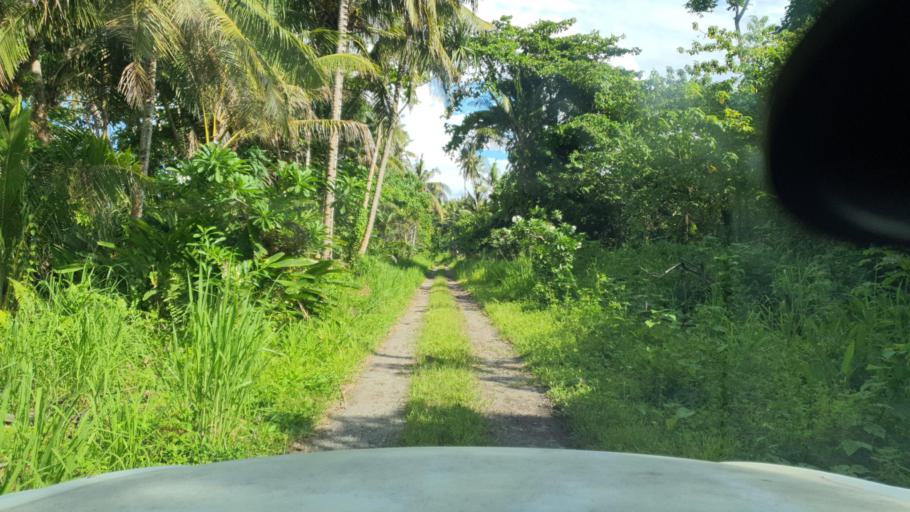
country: SB
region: Guadalcanal
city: Honiara
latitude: -9.2860
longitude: 159.7627
